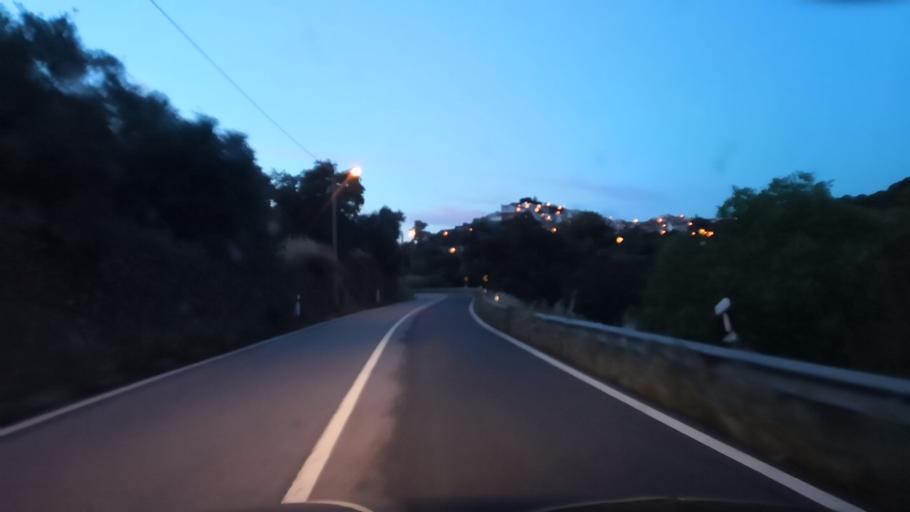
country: ES
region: Extremadura
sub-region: Provincia de Caceres
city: Piedras Albas
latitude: 39.8199
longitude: -6.9829
